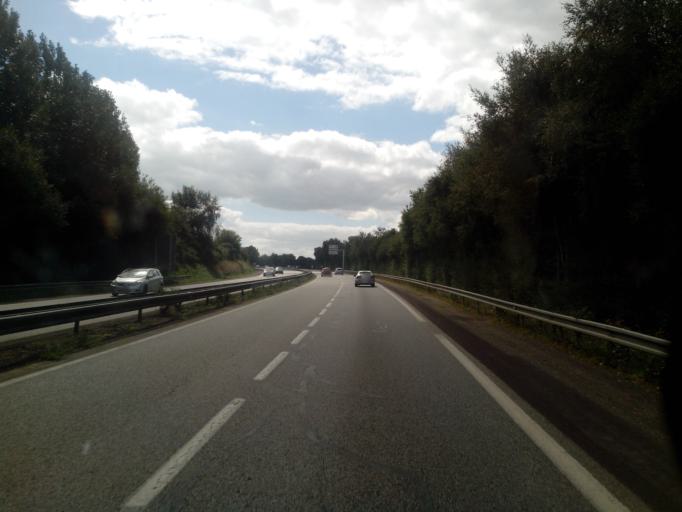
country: FR
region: Brittany
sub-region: Departement du Morbihan
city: Guegon
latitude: 47.9393
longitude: -2.6205
